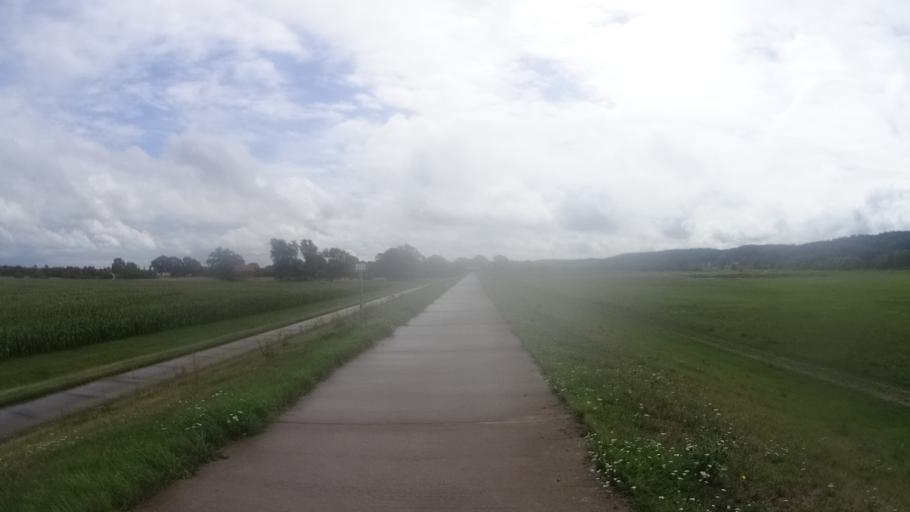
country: DE
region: Lower Saxony
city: Neu Darchau
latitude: 53.2281
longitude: 10.9311
